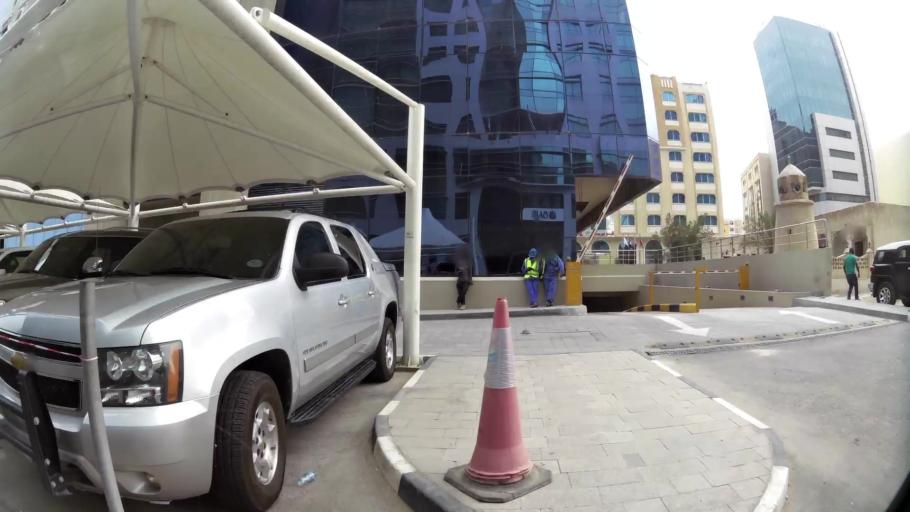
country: QA
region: Baladiyat ad Dawhah
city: Doha
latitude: 25.2882
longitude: 51.5467
